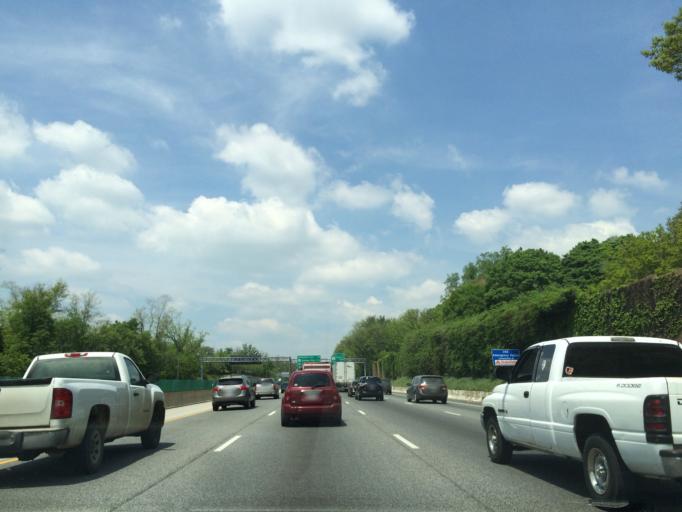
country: US
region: Maryland
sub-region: Baltimore County
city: Charlestown
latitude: 39.2681
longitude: -76.7167
